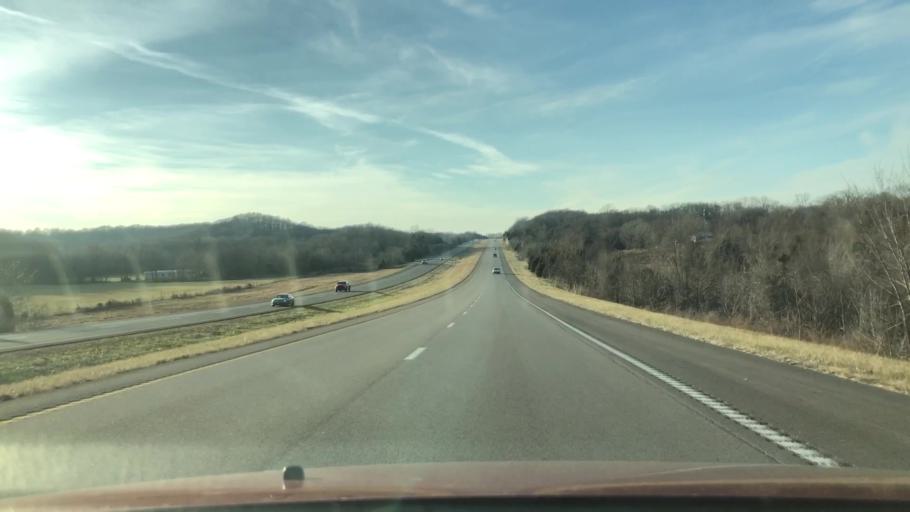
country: US
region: Missouri
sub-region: Wright County
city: Mansfield
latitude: 37.1115
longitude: -92.6526
